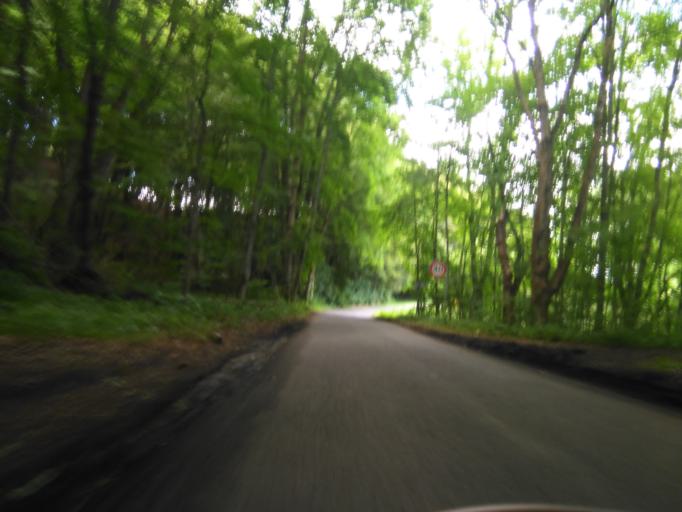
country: DK
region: Central Jutland
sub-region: Skanderborg Kommune
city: Horning
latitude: 56.1018
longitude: 10.0168
